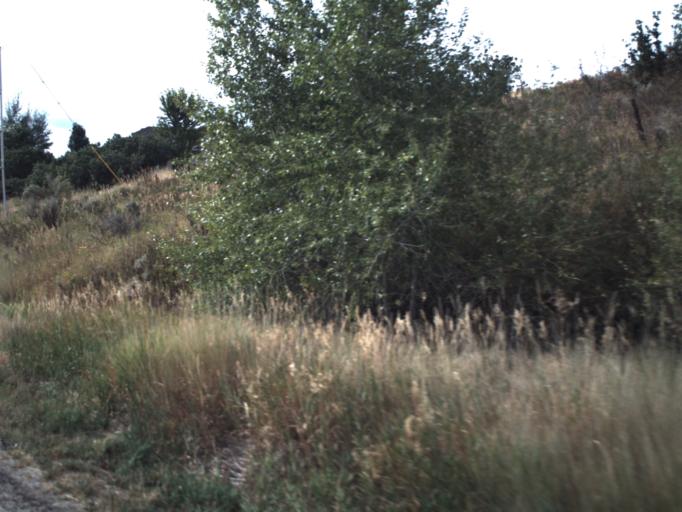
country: US
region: Utah
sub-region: Morgan County
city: Morgan
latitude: 40.9619
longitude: -111.6691
